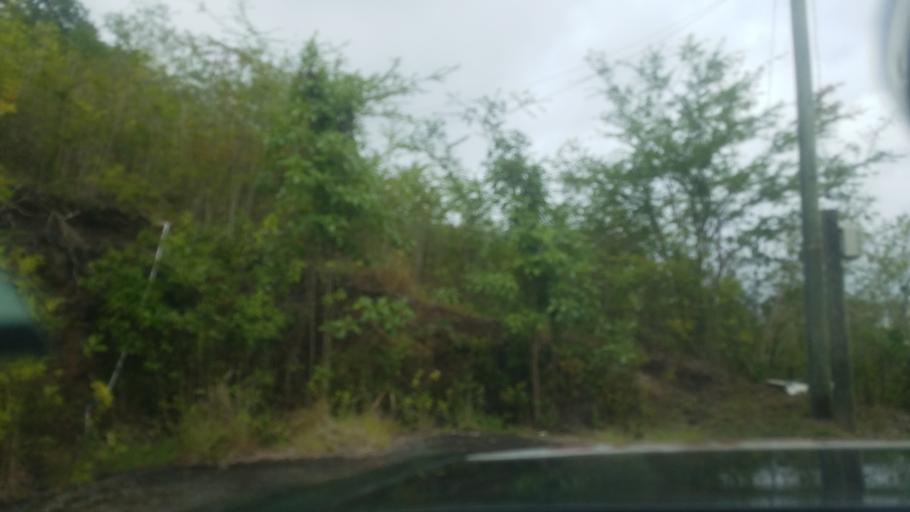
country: LC
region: Laborie Quarter
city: Laborie
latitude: 13.7427
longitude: -60.9675
